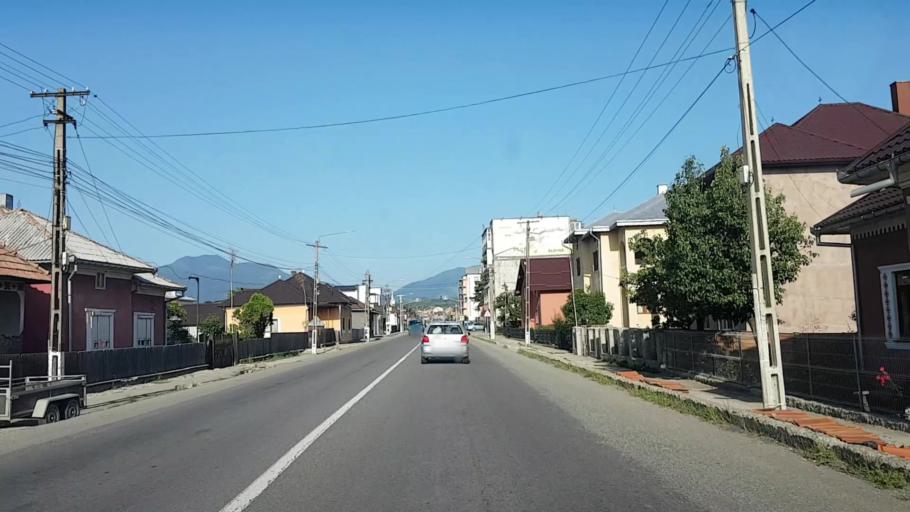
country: RO
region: Bistrita-Nasaud
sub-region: Comuna Prundu Bargaului
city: Susenii Bargaului
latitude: 47.2205
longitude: 24.7262
